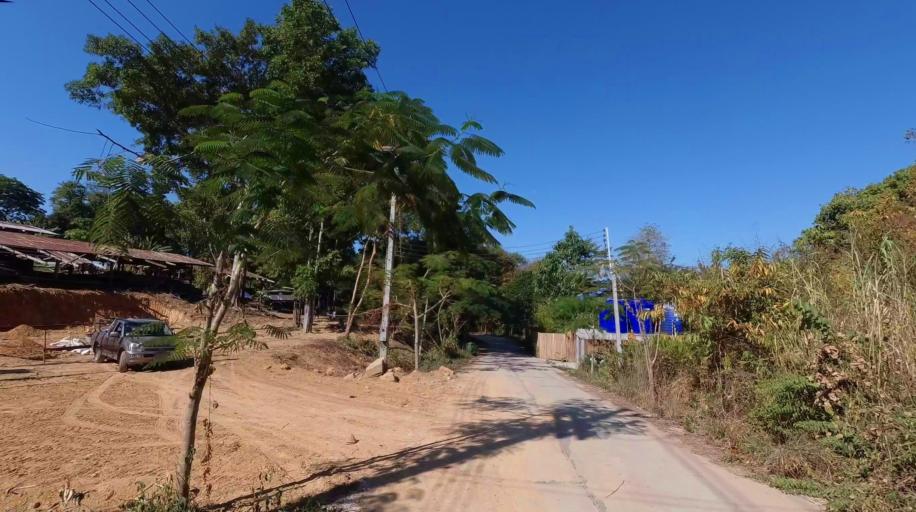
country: TH
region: Trat
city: Ko Kut
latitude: 11.6181
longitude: 102.5370
